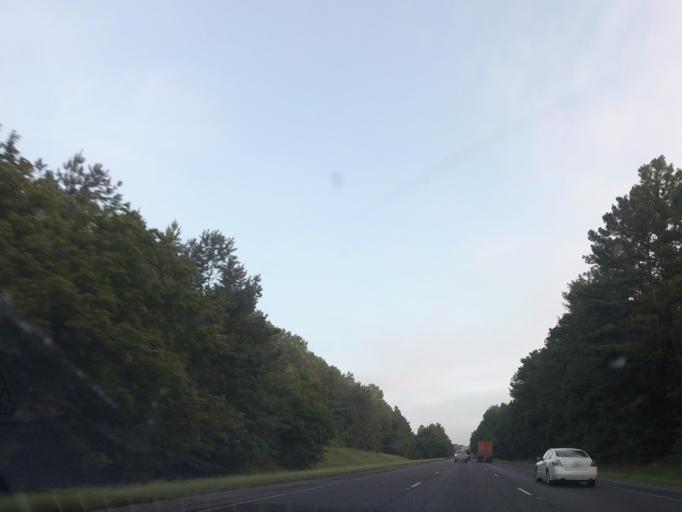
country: US
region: Georgia
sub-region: Monroe County
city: Forsyth
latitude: 33.0894
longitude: -83.9941
